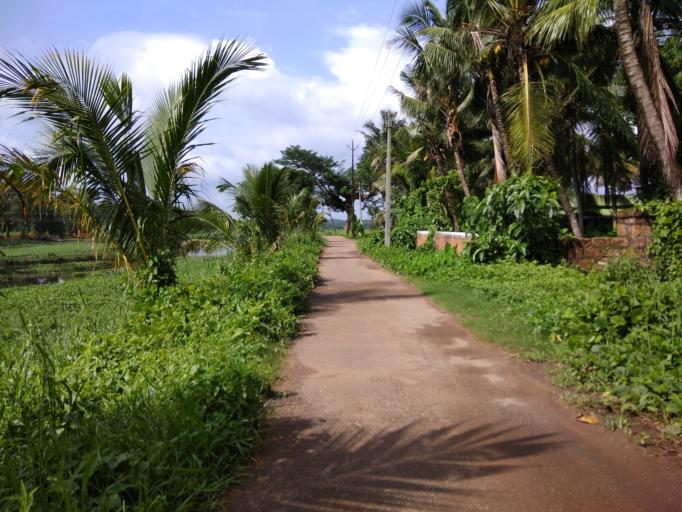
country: IN
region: Kerala
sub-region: Thrissur District
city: Trichur
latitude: 10.5431
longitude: 76.1785
